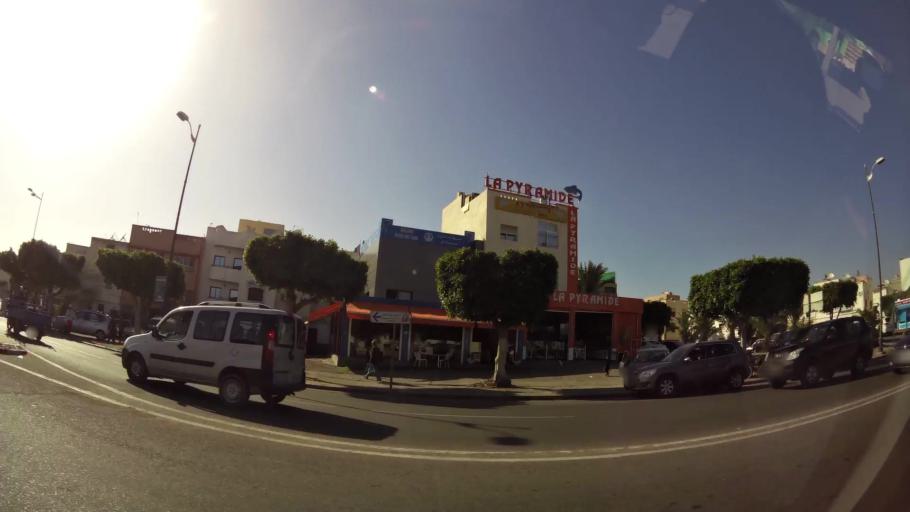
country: MA
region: Oued ed Dahab-Lagouira
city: Dakhla
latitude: 30.4149
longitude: -9.5687
